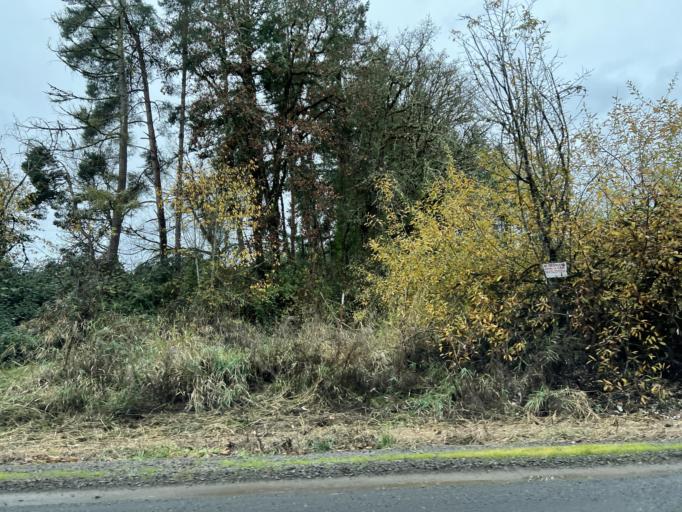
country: US
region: Oregon
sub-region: Polk County
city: Independence
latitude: 44.8134
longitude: -123.0867
